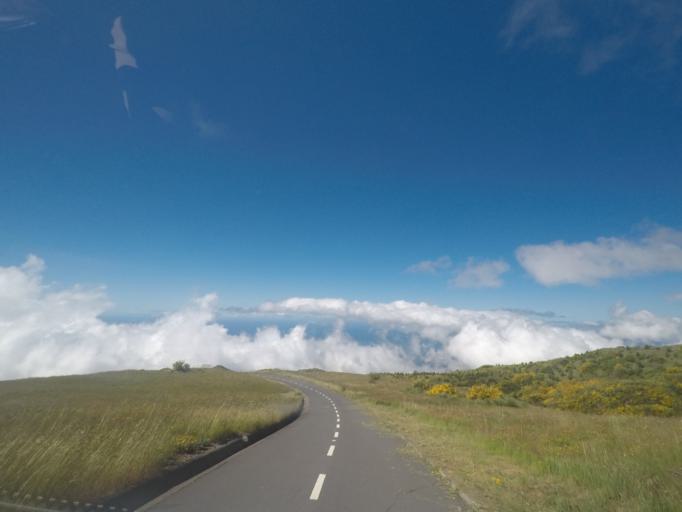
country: PT
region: Madeira
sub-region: Camara de Lobos
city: Curral das Freiras
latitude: 32.7135
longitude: -16.9383
